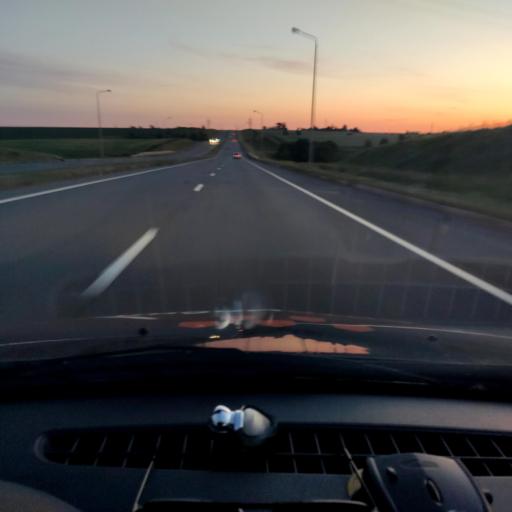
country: RU
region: Belgorod
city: Staryy Oskol
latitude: 51.3249
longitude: 37.7271
